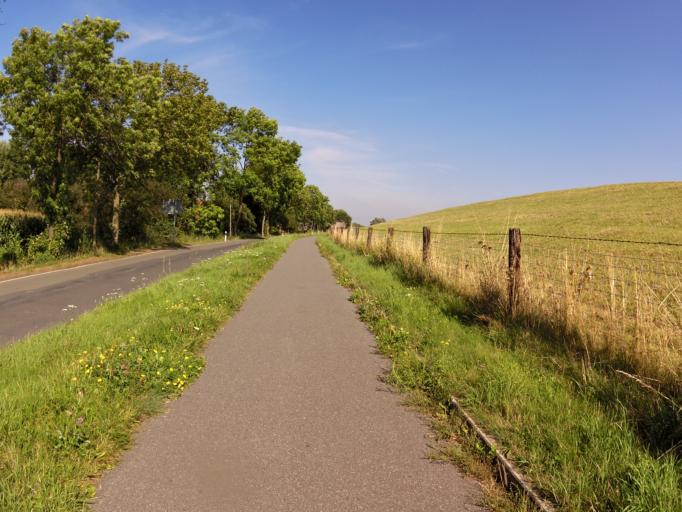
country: DE
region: Lower Saxony
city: Elsfleth
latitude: 53.2778
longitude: 8.4806
